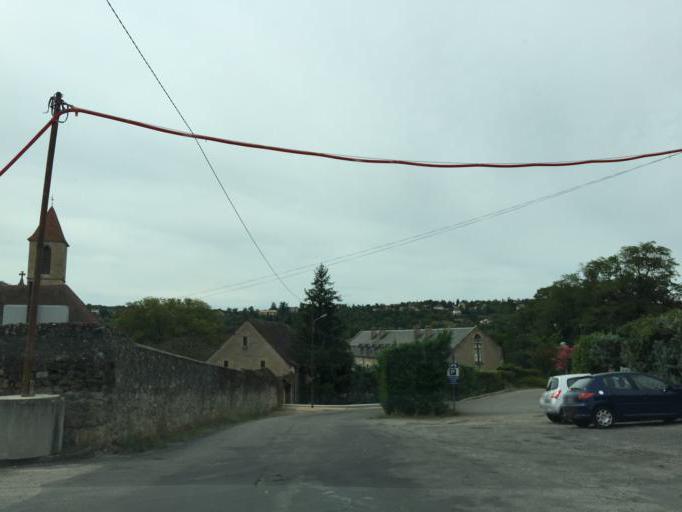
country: FR
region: Midi-Pyrenees
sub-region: Departement de l'Aveyron
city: Villefranche-de-Rouergue
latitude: 44.3441
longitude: 2.0343
